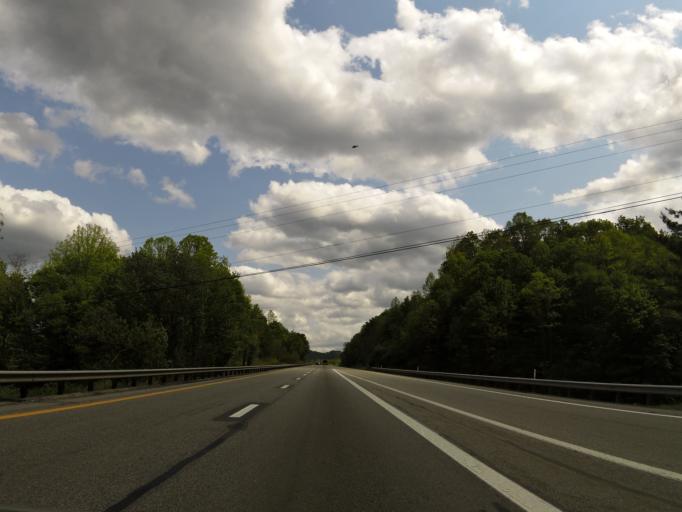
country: US
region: West Virginia
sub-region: Raleigh County
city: Bradley
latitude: 37.9136
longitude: -81.2694
